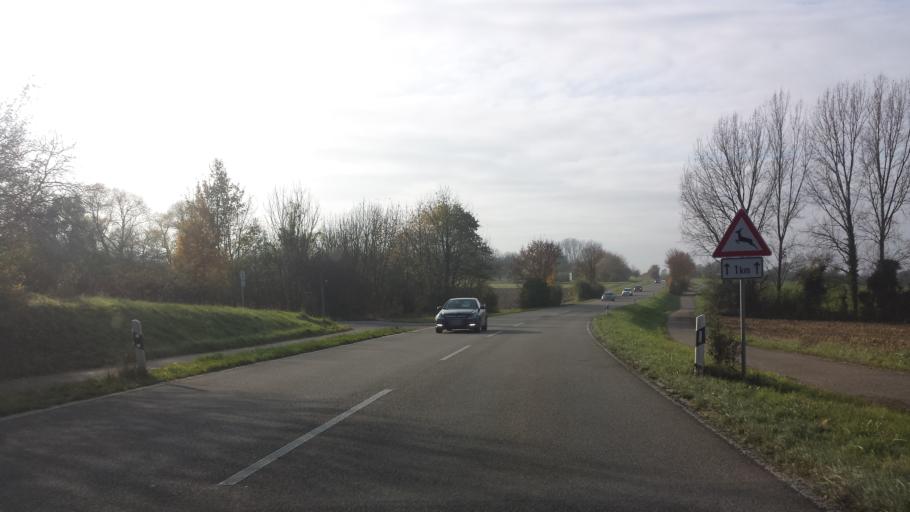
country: DE
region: Baden-Wuerttemberg
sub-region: Karlsruhe Region
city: Ubstadt-Weiher
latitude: 49.1750
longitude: 8.6408
